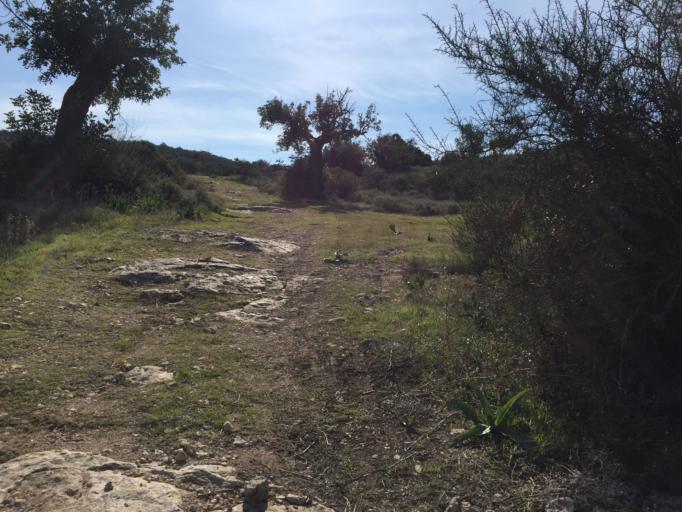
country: CY
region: Limassol
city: Mouttagiaka
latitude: 34.7455
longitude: 33.1140
